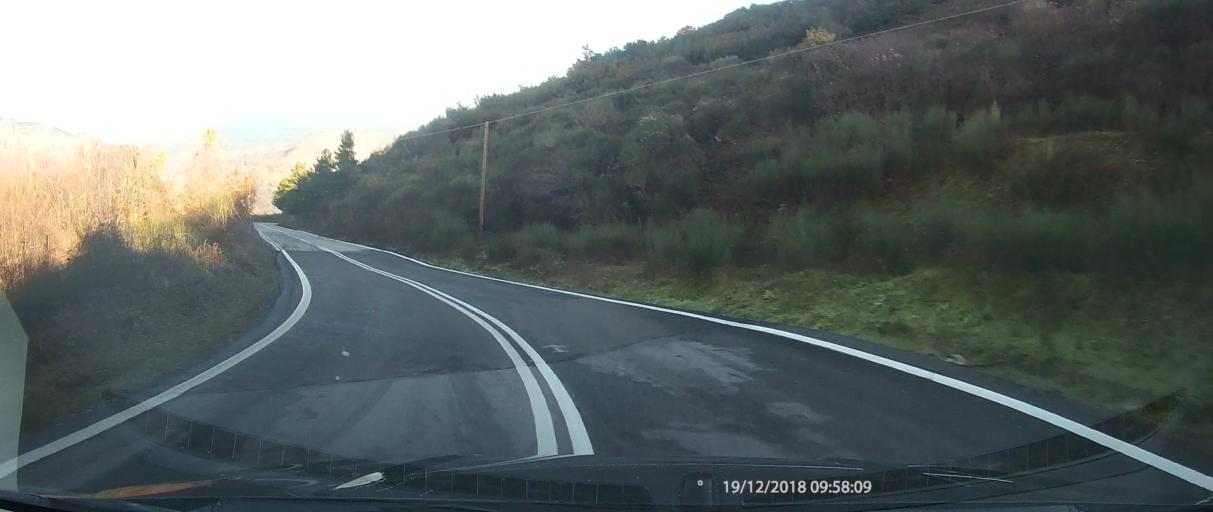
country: GR
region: Peloponnese
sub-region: Nomos Messinias
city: Paralia Vergas
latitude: 37.0885
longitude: 22.2360
